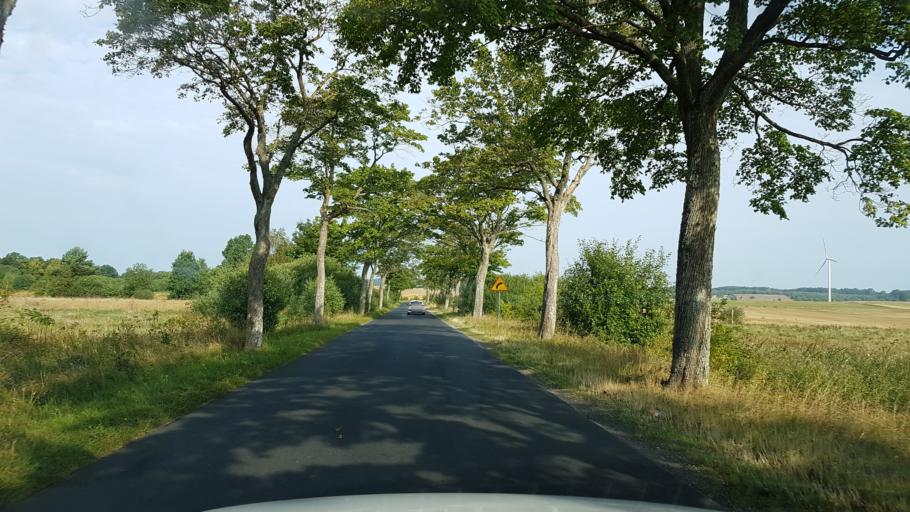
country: PL
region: West Pomeranian Voivodeship
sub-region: Powiat slawienski
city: Slawno
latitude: 54.4553
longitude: 16.5913
